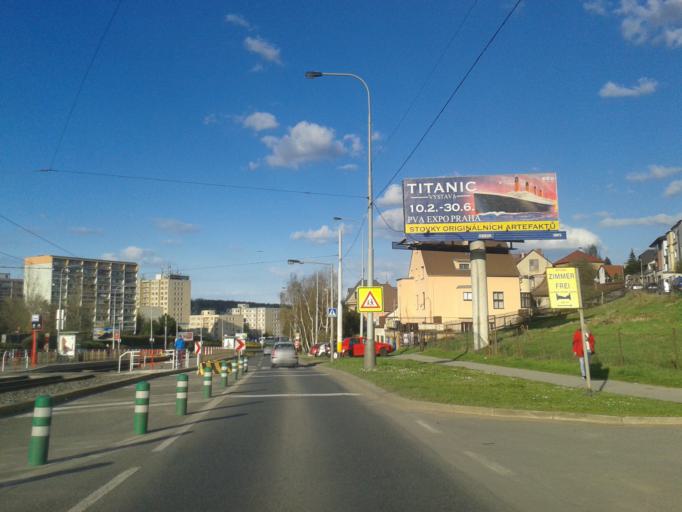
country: CZ
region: Central Bohemia
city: Hostivice
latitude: 50.0633
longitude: 14.3151
